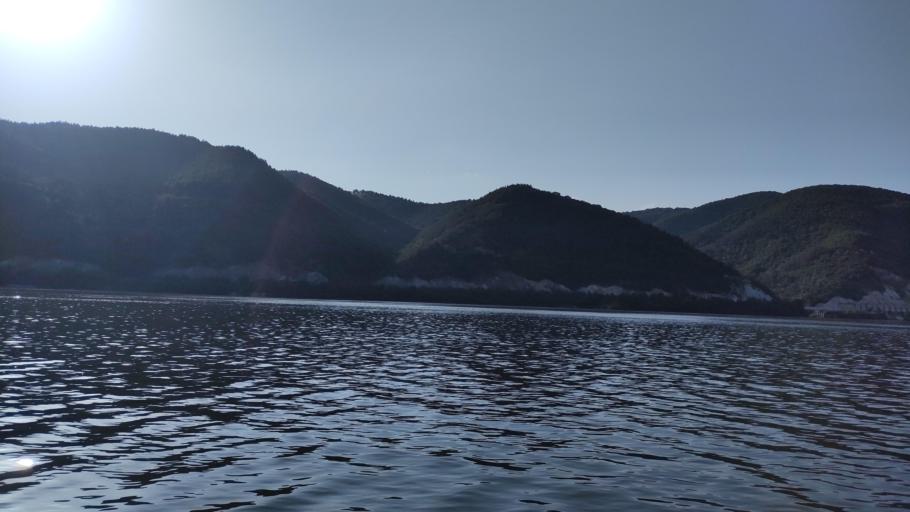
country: RO
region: Mehedinti
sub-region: Comuna Dubova
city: Dubova
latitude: 44.5347
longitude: 22.2152
